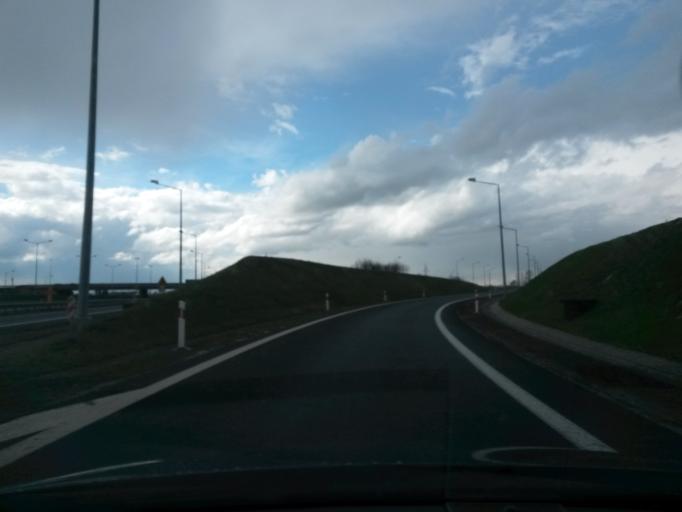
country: PL
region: Greater Poland Voivodeship
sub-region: Powiat poznanski
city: Daszewice
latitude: 52.3459
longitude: 17.0036
